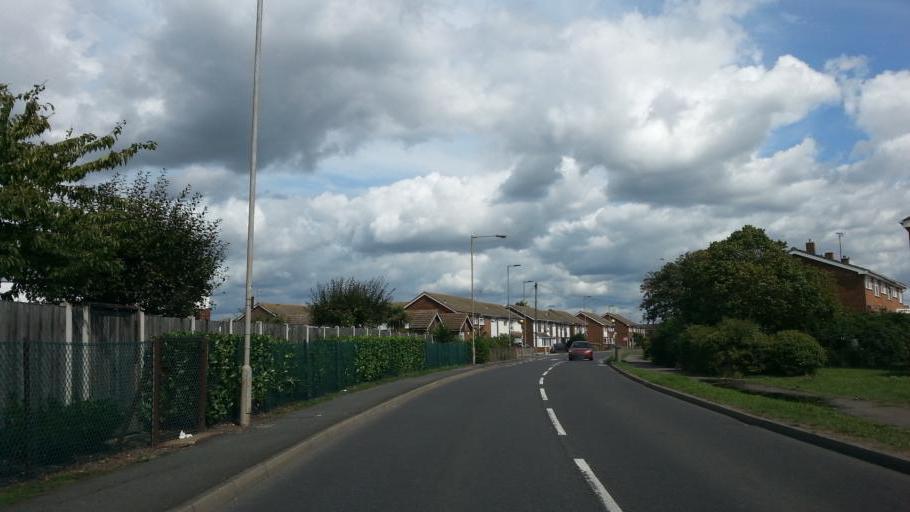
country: GB
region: England
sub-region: Essex
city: Canvey Island
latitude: 51.5241
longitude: 0.5681
